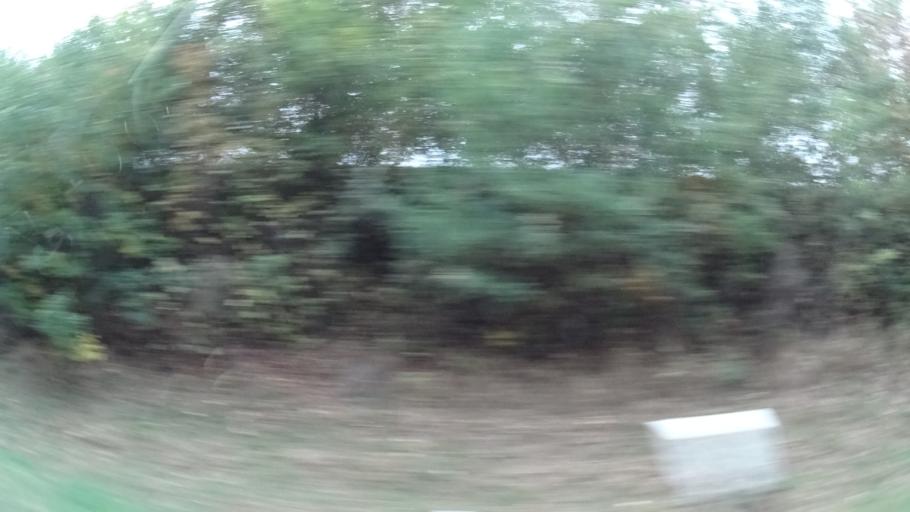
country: DE
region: Hesse
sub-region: Regierungsbezirk Kassel
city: Flieden
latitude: 50.4331
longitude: 9.5901
